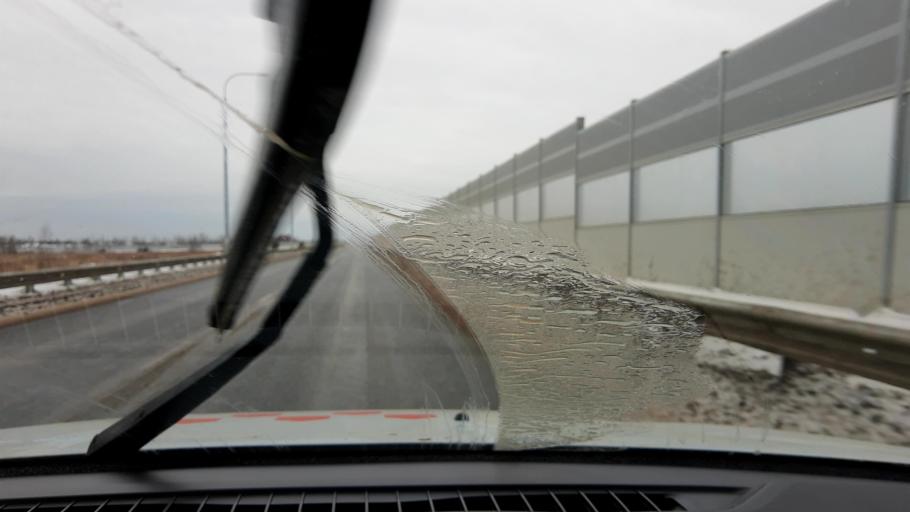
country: RU
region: Nizjnij Novgorod
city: Neklyudovo
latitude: 56.4263
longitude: 43.9726
